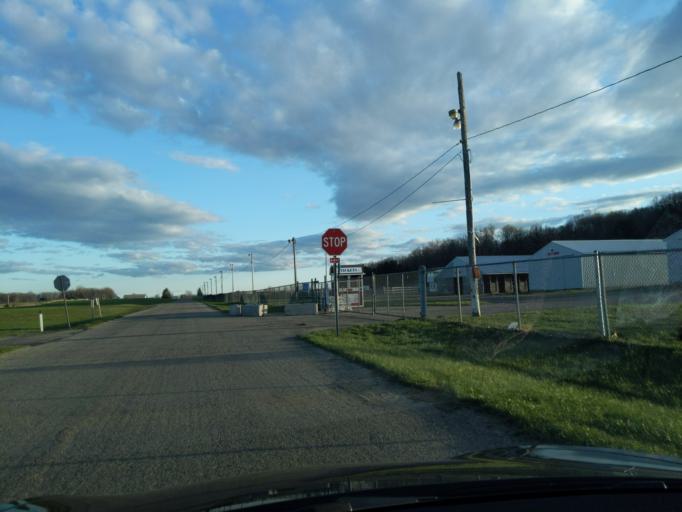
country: US
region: Michigan
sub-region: Ingham County
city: Mason
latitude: 42.5724
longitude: -84.4281
